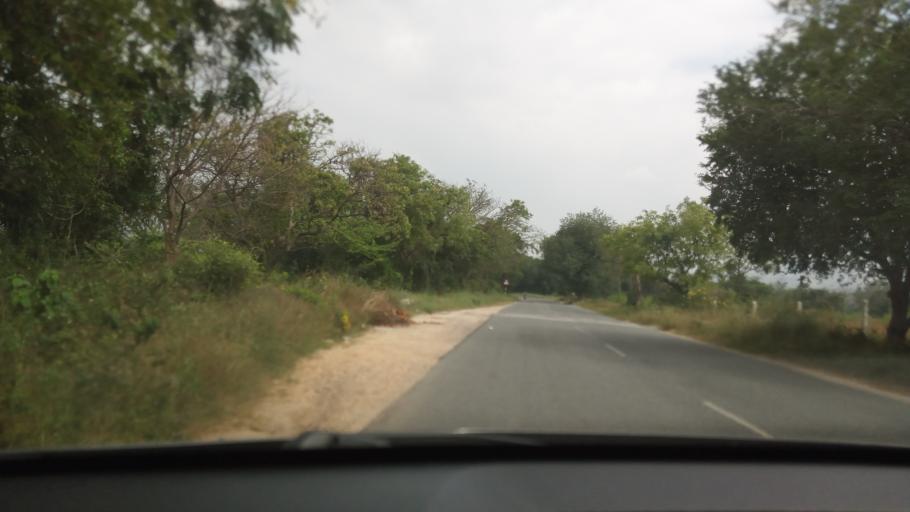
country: IN
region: Andhra Pradesh
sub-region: Chittoor
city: Madanapalle
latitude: 13.6519
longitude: 78.8277
